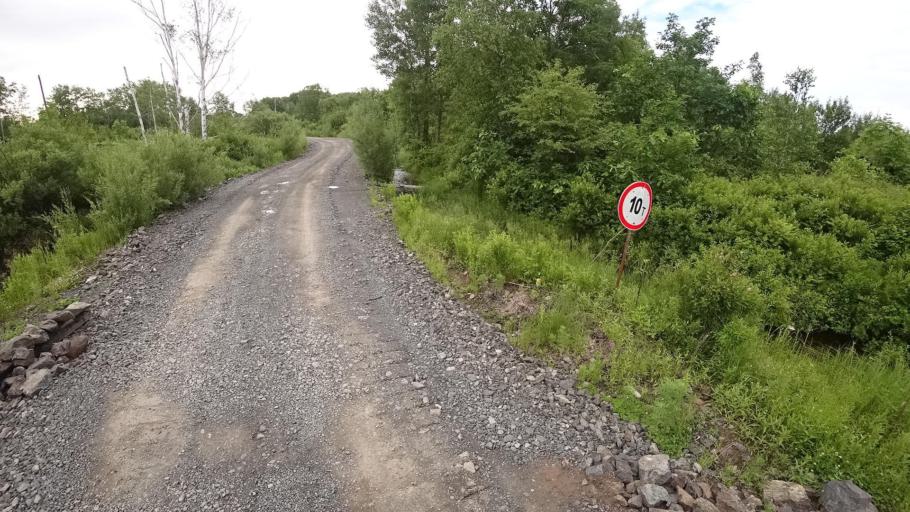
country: RU
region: Khabarovsk Krai
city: Amursk
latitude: 49.8954
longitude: 136.1217
